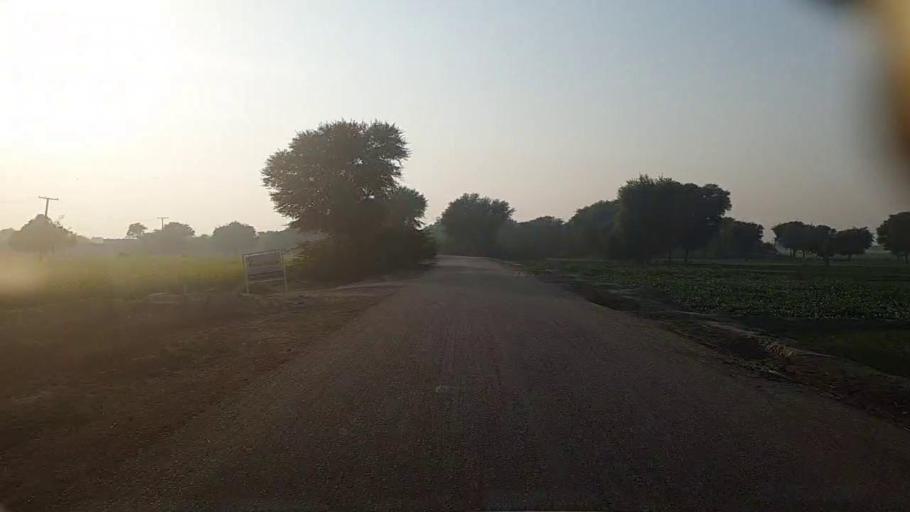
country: PK
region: Sindh
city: Pad Idan
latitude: 26.7180
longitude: 68.4072
